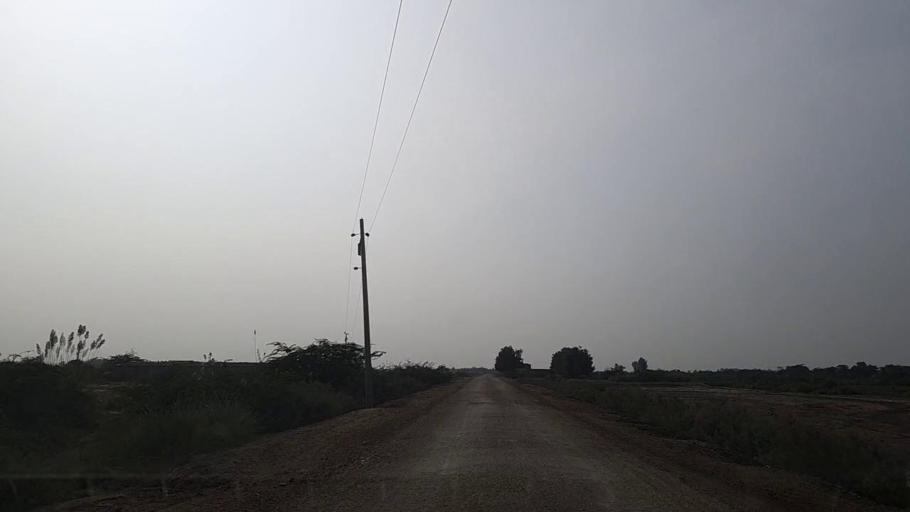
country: PK
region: Sindh
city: Mirpur Sakro
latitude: 24.6439
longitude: 67.6090
